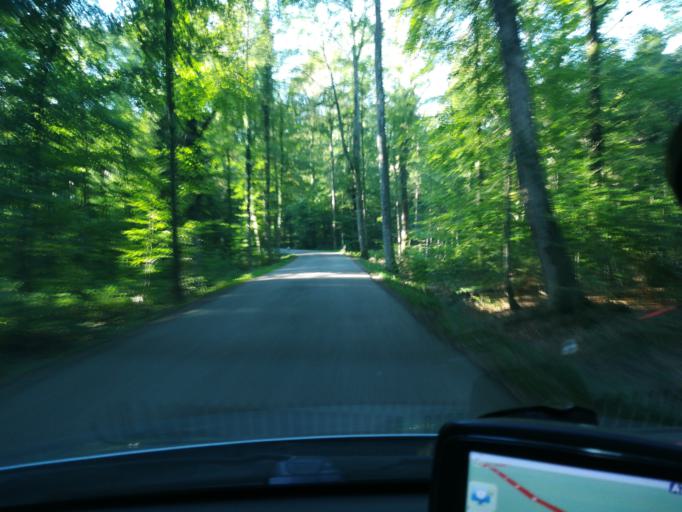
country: CH
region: Thurgau
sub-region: Kreuzlingen District
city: Ermatingen
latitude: 47.6505
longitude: 9.0785
